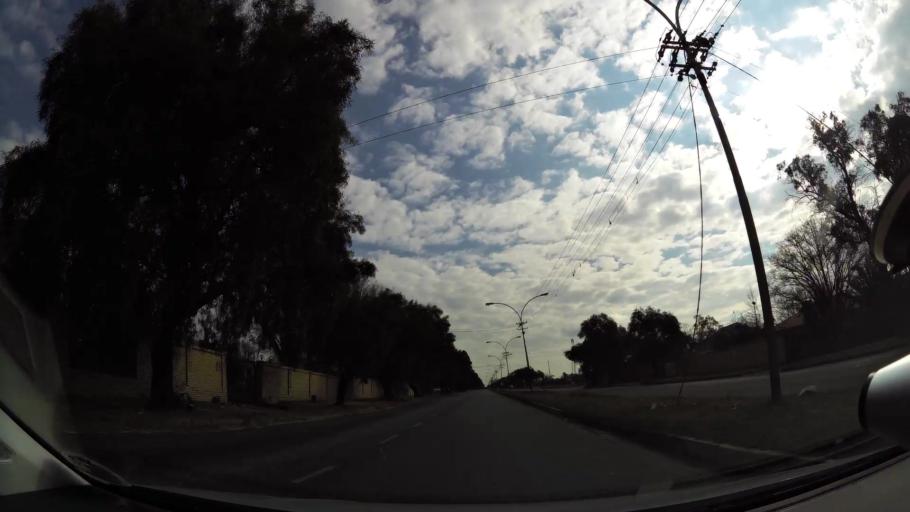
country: ZA
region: Orange Free State
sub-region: Mangaung Metropolitan Municipality
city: Bloemfontein
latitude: -29.0907
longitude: 26.2459
